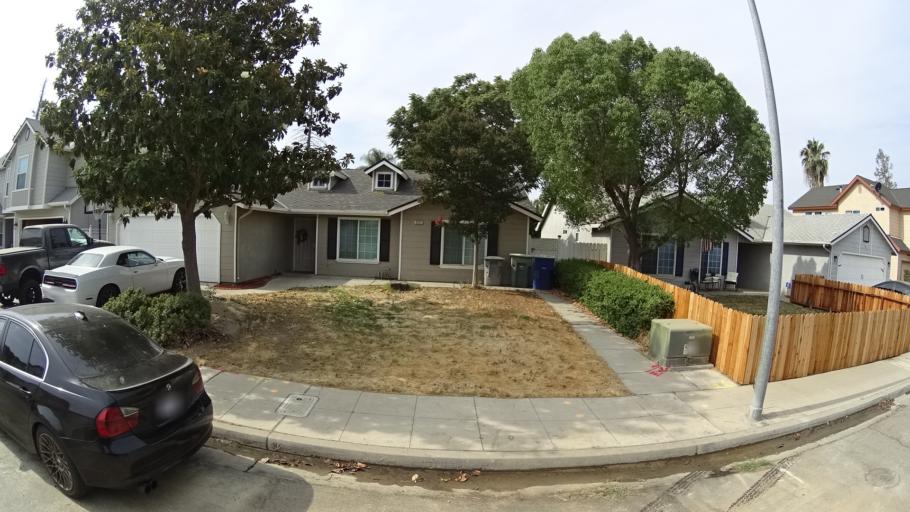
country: US
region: California
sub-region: Fresno County
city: West Park
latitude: 36.7704
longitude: -119.8772
